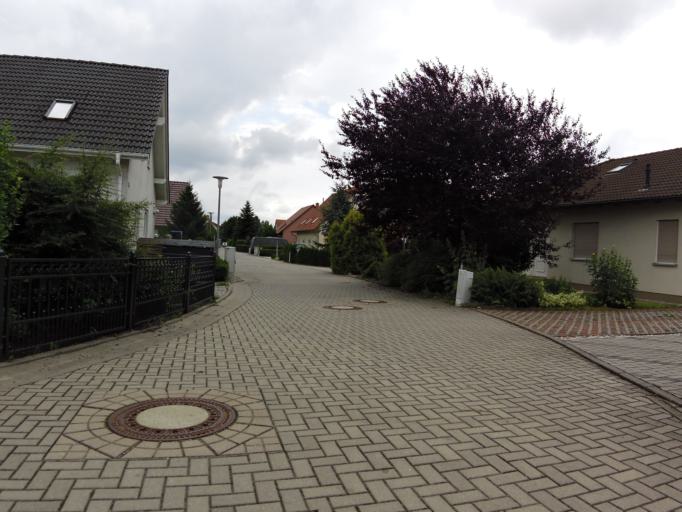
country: DE
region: Saxony
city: Taucha
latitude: 51.3520
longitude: 12.4854
